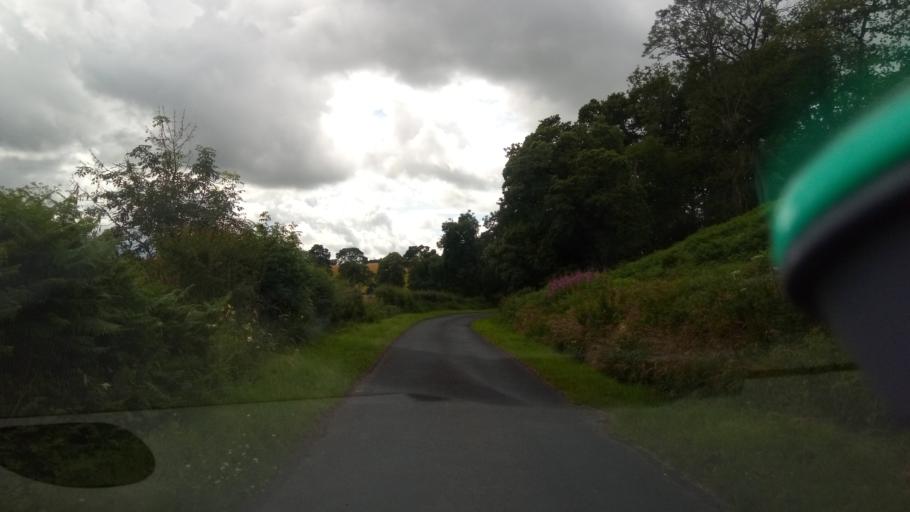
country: GB
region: Scotland
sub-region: The Scottish Borders
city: Kelso
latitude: 55.4877
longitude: -2.4310
